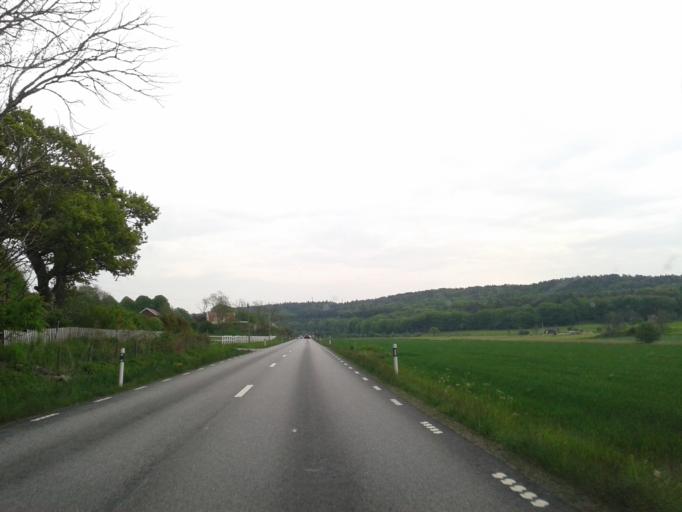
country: SE
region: Vaestra Goetaland
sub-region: Kungalvs Kommun
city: Kode
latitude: 57.8909
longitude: 11.7685
